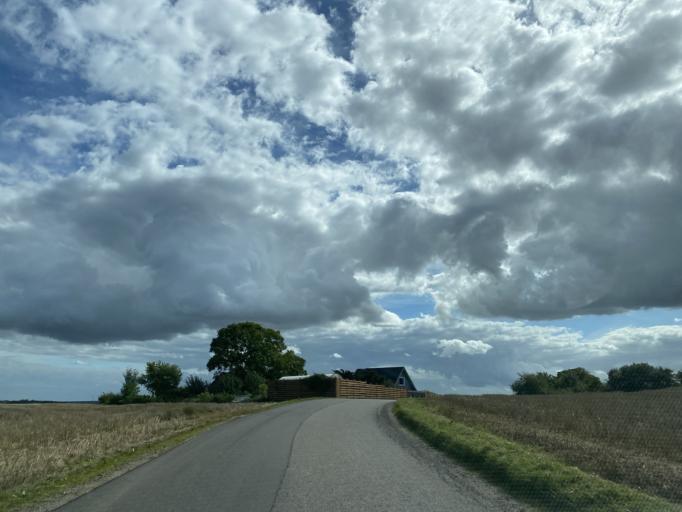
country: DK
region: Central Jutland
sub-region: Skanderborg Kommune
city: Skanderborg
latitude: 55.9759
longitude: 9.8563
